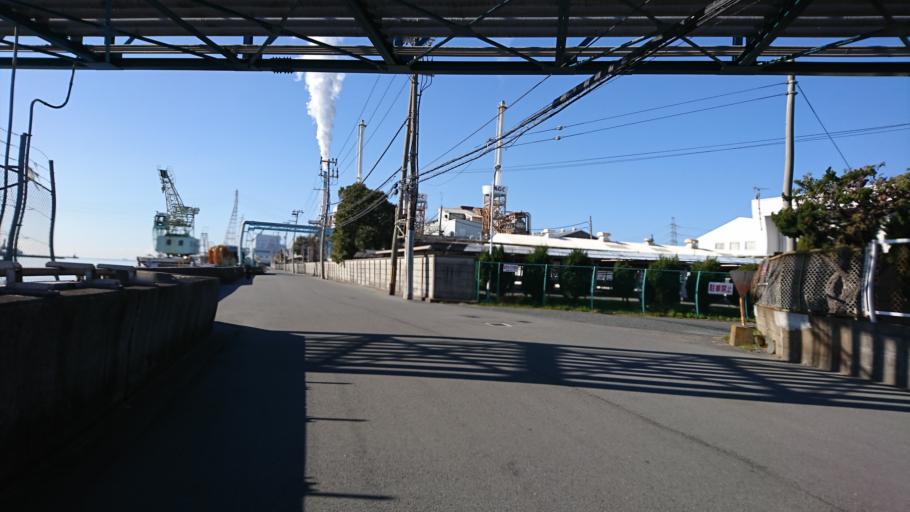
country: JP
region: Hyogo
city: Kakogawacho-honmachi
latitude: 34.7609
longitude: 134.7734
